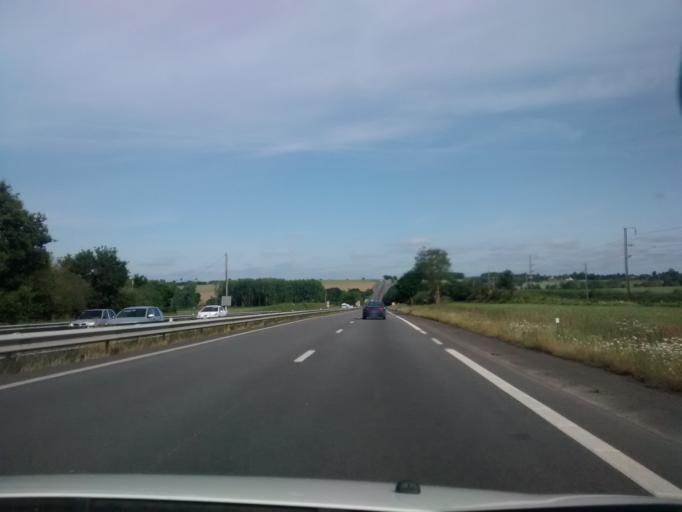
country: FR
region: Brittany
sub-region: Departement des Cotes-d'Armor
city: Sevignac
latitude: 48.3554
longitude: -2.3099
